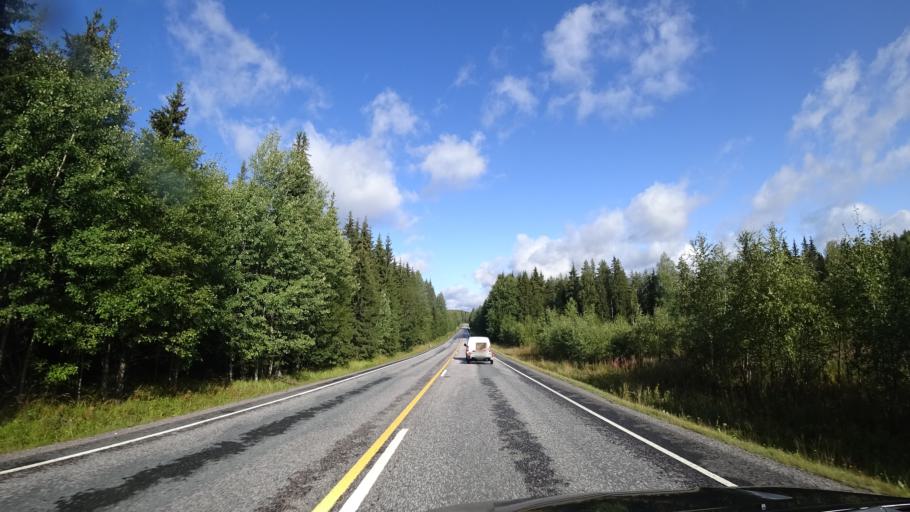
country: FI
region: Uusimaa
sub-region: Helsinki
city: Tuusula
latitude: 60.4534
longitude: 24.9553
